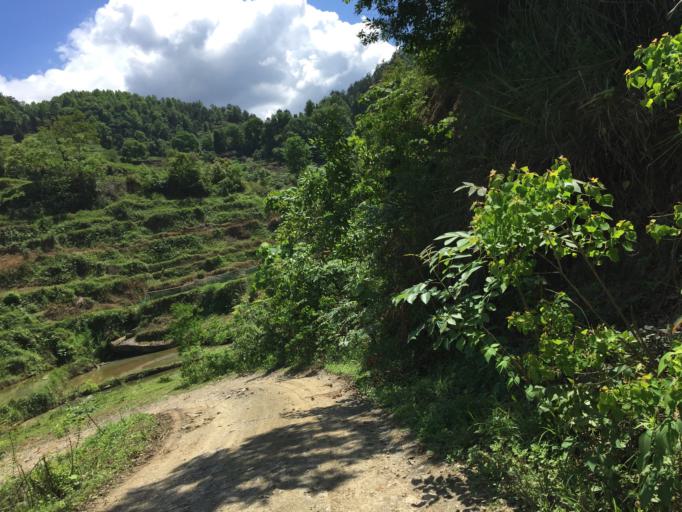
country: CN
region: Guizhou Sheng
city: Shiqian
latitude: 27.6754
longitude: 108.0817
